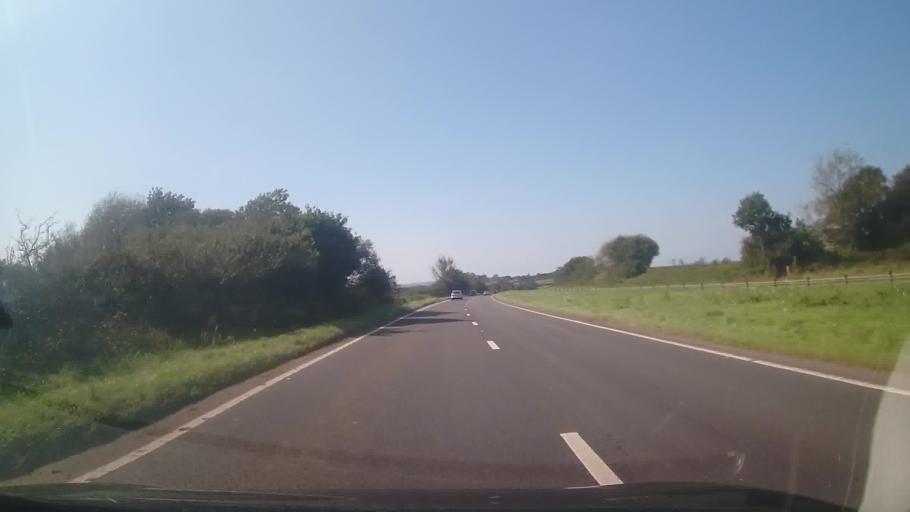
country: GB
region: Wales
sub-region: Carmarthenshire
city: Llangynog
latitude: 51.8279
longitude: -4.4484
